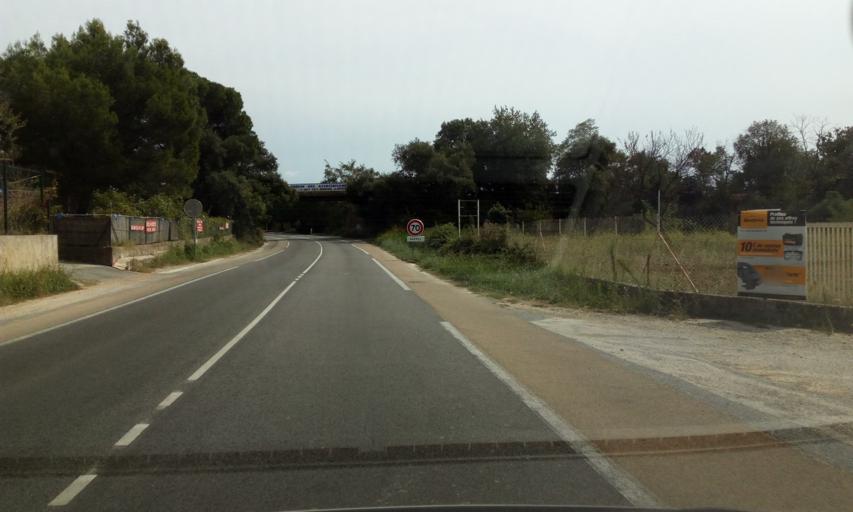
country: FR
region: Provence-Alpes-Cote d'Azur
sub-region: Departement du Var
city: Bormes-les-Mimosas
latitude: 43.1477
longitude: 6.3197
